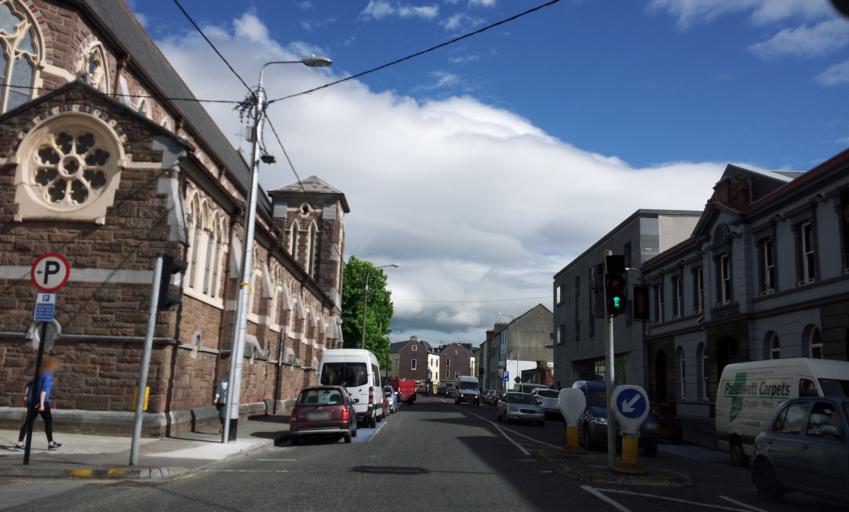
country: IE
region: Munster
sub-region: Ciarrai
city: Tralee
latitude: 52.2675
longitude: -9.7095
